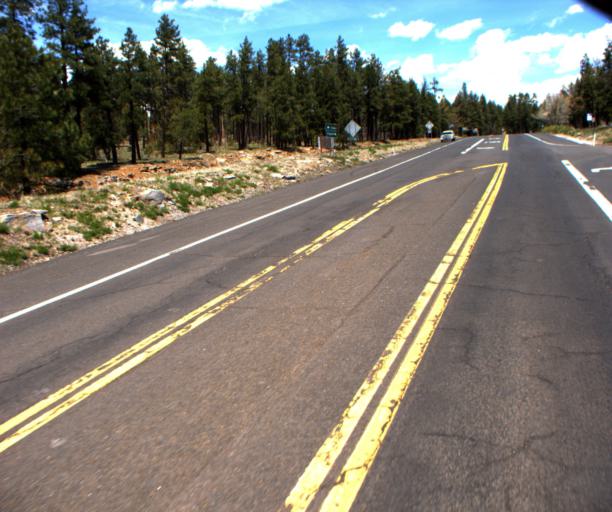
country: US
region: Arizona
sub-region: Coconino County
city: Kachina Village
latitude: 35.0315
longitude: -111.7340
